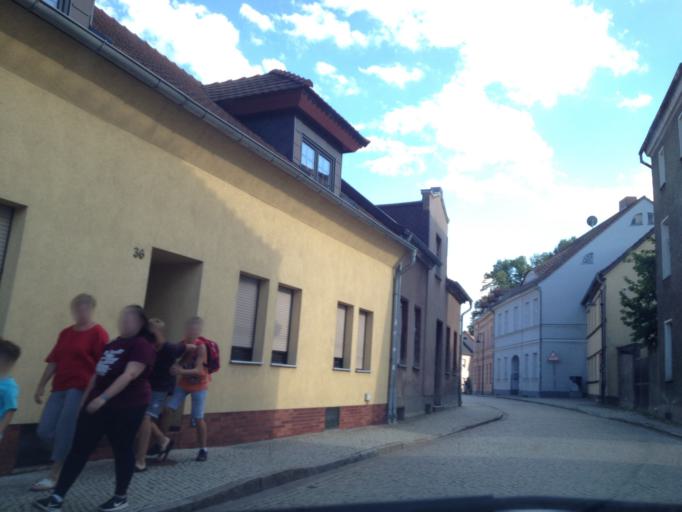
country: DE
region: Brandenburg
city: Vetschau
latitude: 51.7840
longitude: 14.0718
